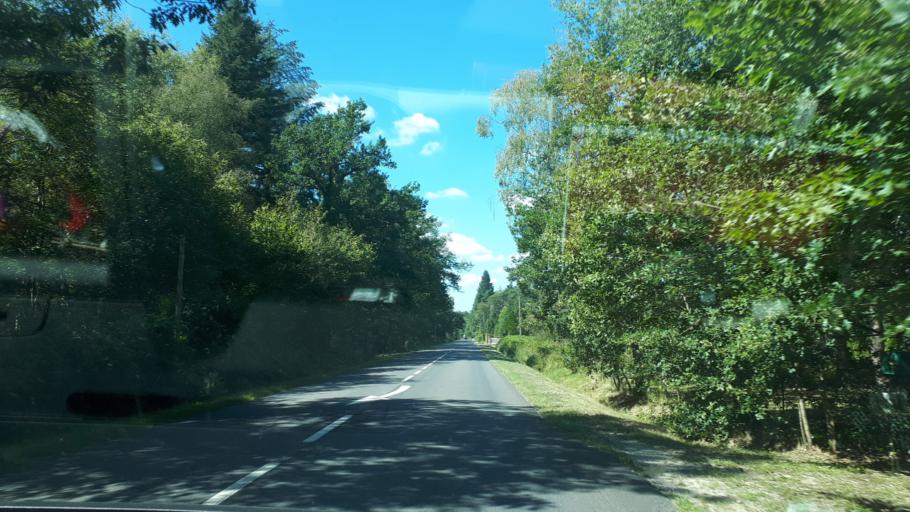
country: FR
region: Centre
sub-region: Departement du Loir-et-Cher
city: Lamotte-Beuvron
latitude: 47.5902
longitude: 2.0051
